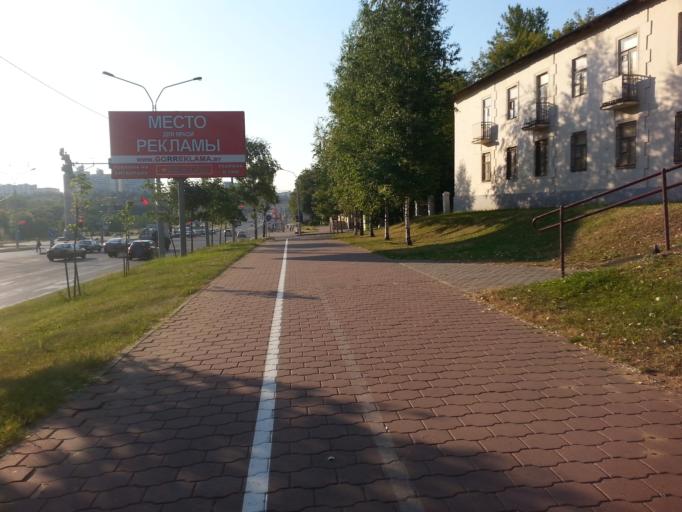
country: BY
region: Minsk
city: Vyaliki Trastsyanets
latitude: 53.8640
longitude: 27.6659
